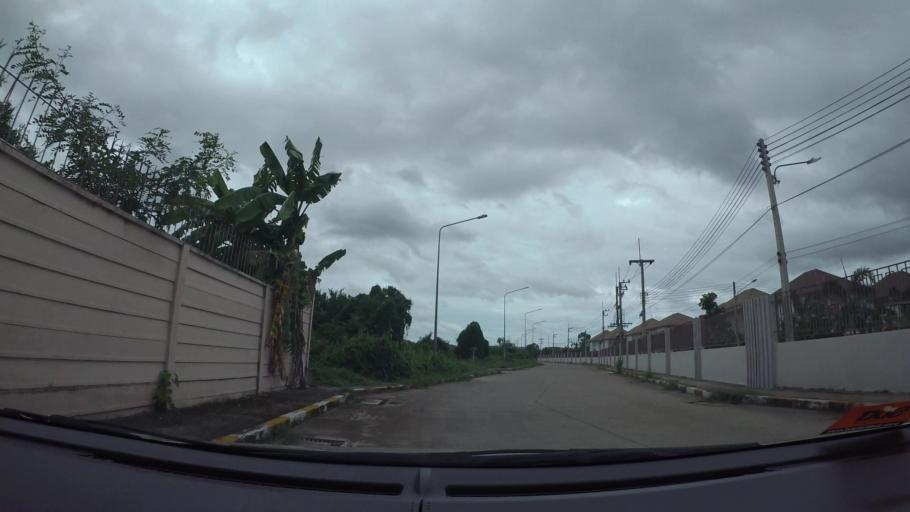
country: TH
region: Chon Buri
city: Sattahip
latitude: 12.7266
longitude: 100.8934
